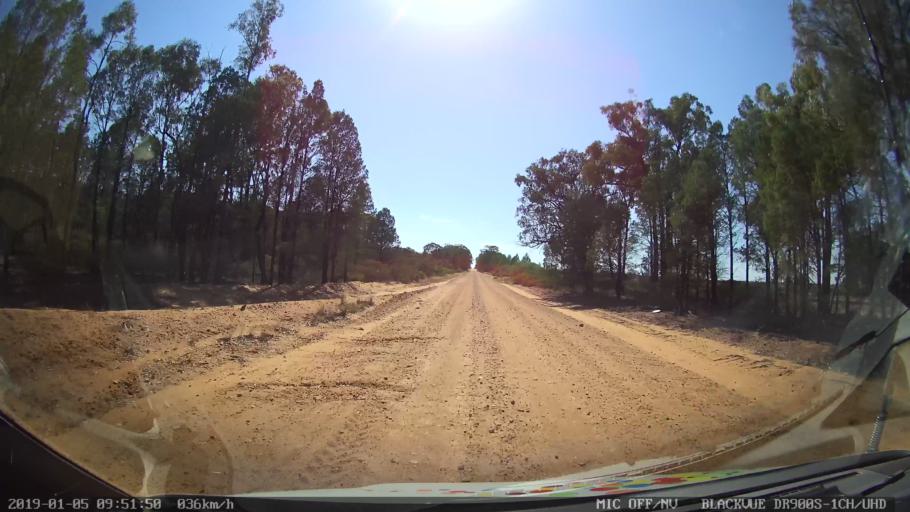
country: AU
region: New South Wales
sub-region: Gilgandra
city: Gilgandra
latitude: -31.6610
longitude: 148.7629
